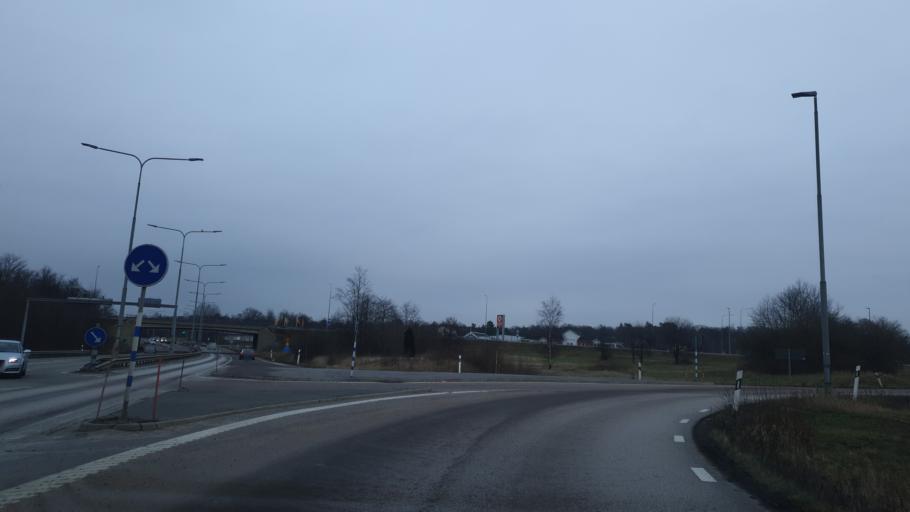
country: SE
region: Blekinge
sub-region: Karlskrona Kommun
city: Rodeby
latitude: 56.2047
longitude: 15.6408
